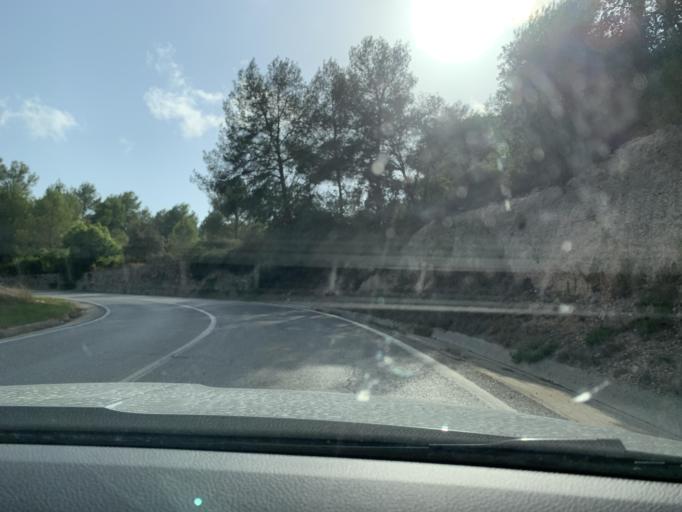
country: ES
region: Catalonia
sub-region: Provincia de Tarragona
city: el Catllar
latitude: 41.1499
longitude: 1.3143
